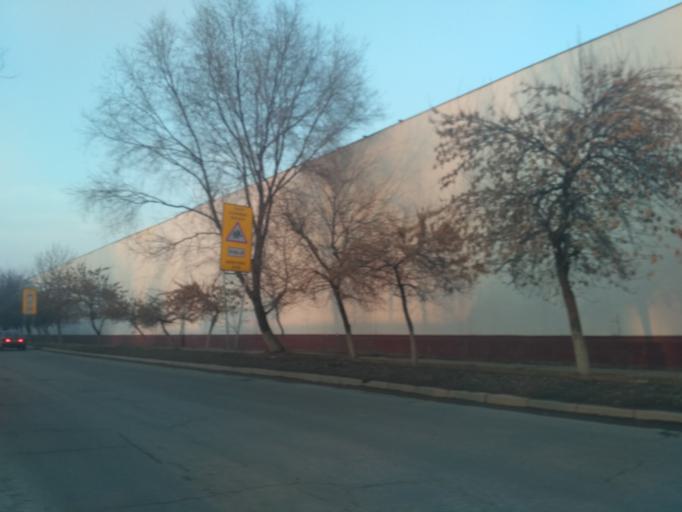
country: KZ
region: Almaty Qalasy
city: Almaty
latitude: 43.2676
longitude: 76.8627
